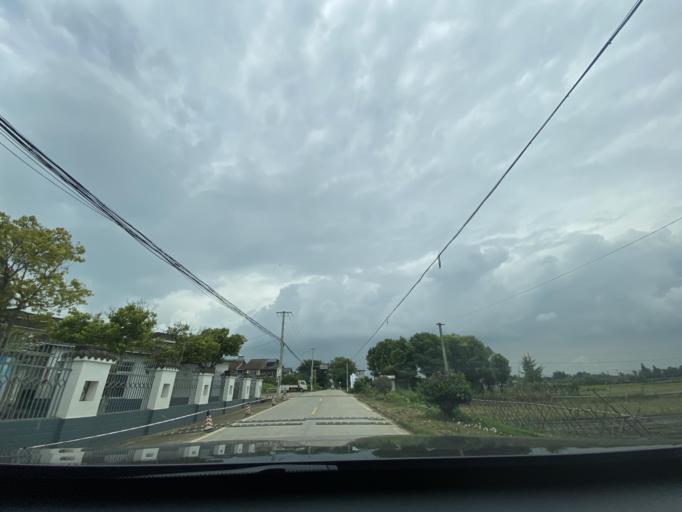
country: CN
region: Sichuan
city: Wujin
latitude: 30.3767
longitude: 103.9683
